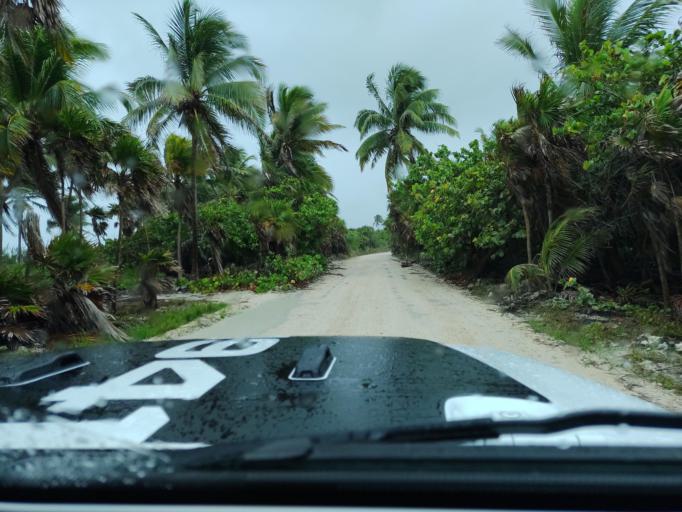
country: MX
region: Quintana Roo
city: Tulum
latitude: 19.9818
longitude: -87.4684
